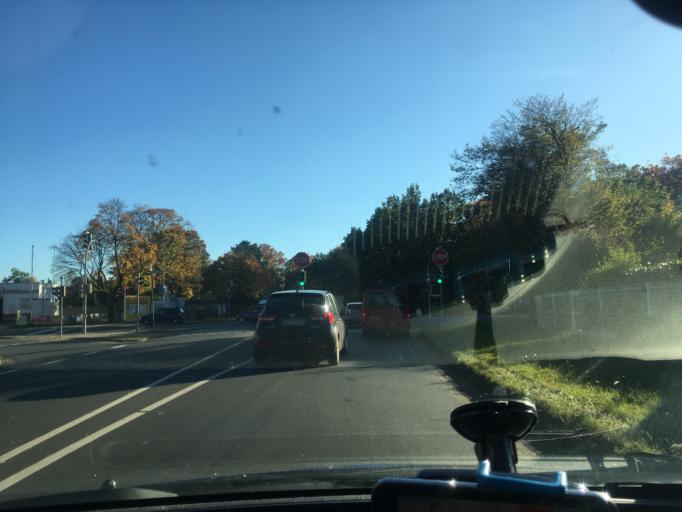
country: DE
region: Lower Saxony
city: Winsen
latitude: 52.6341
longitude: 9.9302
